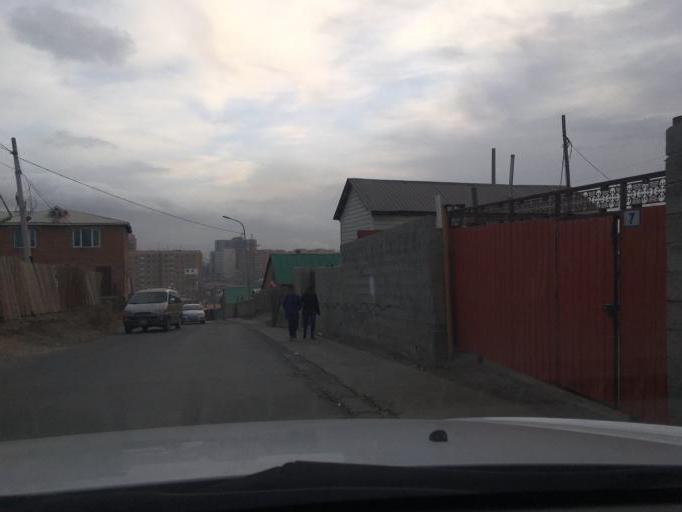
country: MN
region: Ulaanbaatar
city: Ulaanbaatar
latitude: 47.9179
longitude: 106.8331
